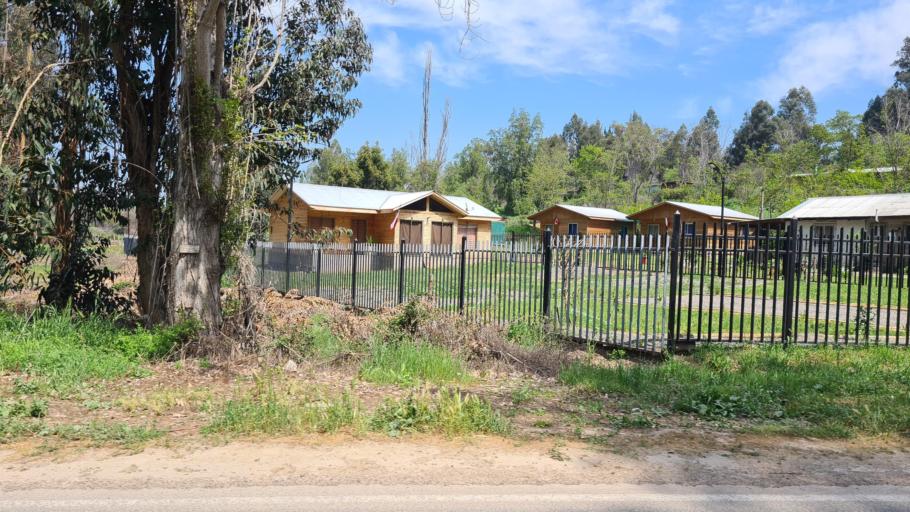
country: CL
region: O'Higgins
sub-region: Provincia de Cachapoal
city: San Vicente
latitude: -34.1587
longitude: -71.4152
